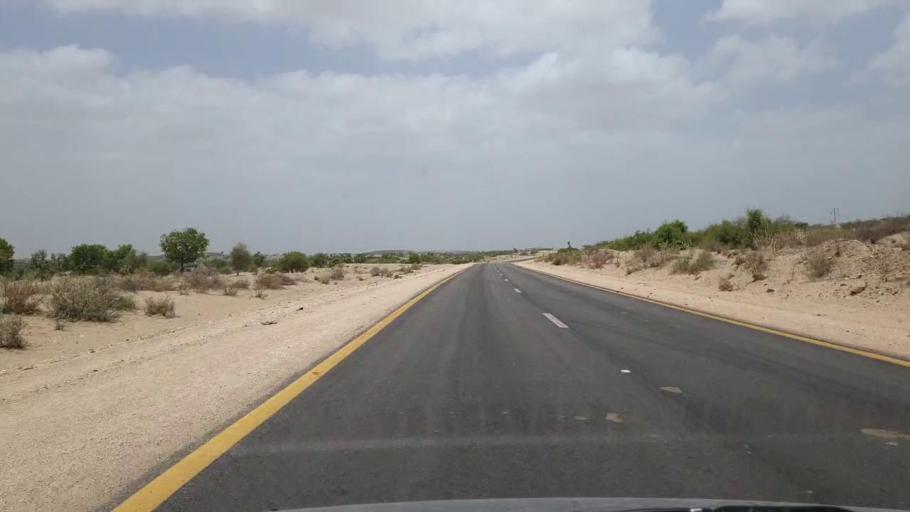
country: PK
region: Sindh
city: Naukot
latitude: 24.8446
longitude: 69.5405
